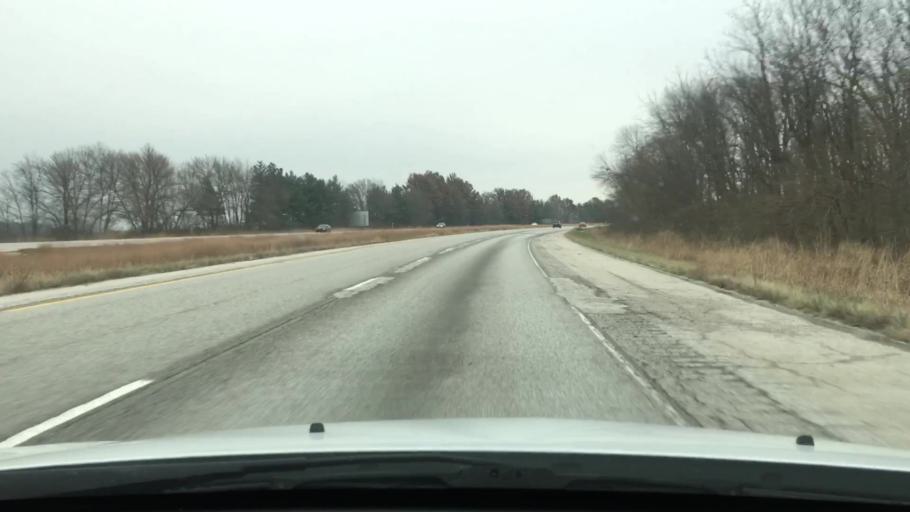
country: US
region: Illinois
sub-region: Morgan County
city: Jacksonville
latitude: 39.7363
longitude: -90.1522
